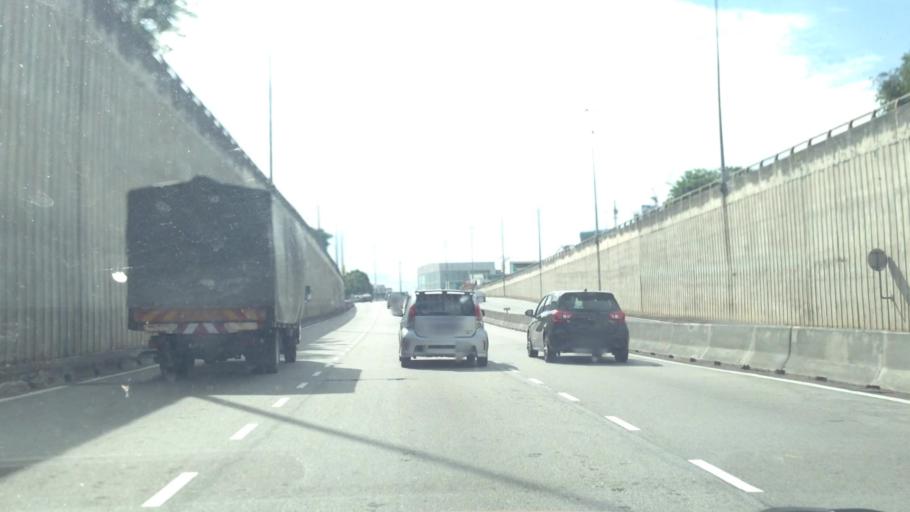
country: MY
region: Selangor
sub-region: Petaling
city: Petaling Jaya
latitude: 3.0746
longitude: 101.6144
